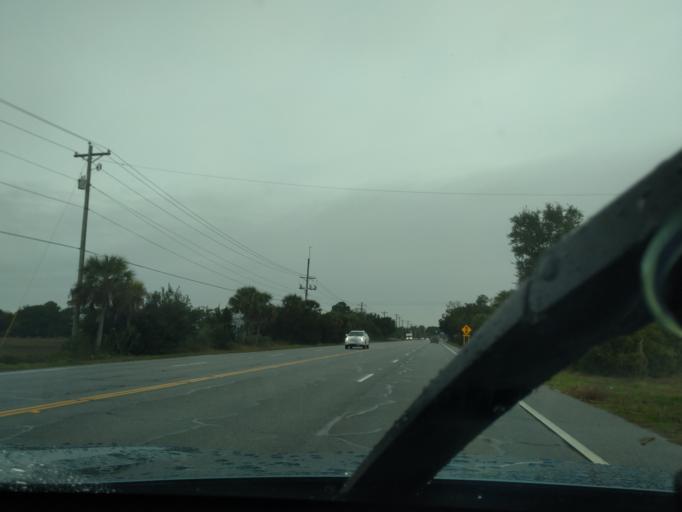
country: US
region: South Carolina
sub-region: Charleston County
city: Folly Beach
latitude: 32.6828
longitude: -79.9572
